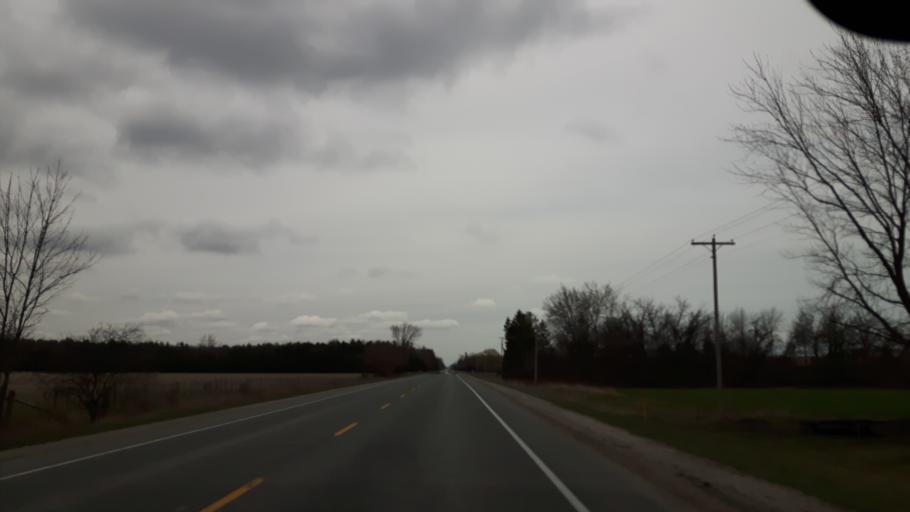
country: CA
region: Ontario
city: Goderich
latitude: 43.6763
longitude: -81.7057
